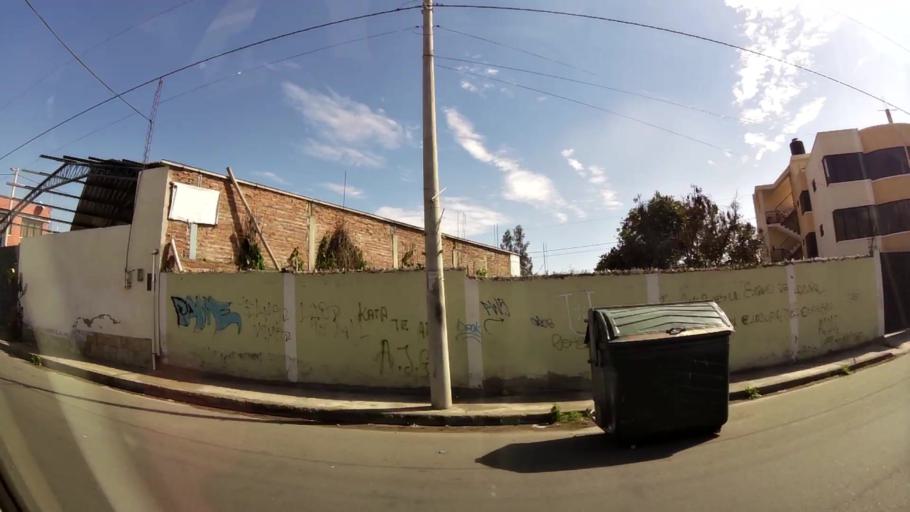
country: EC
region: Chimborazo
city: Riobamba
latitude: -1.6622
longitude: -78.6677
